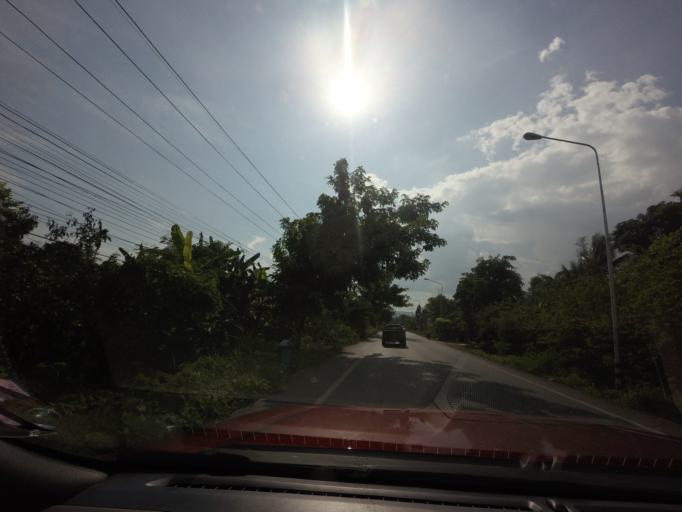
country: TH
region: Yala
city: Yala
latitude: 6.5577
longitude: 101.2219
